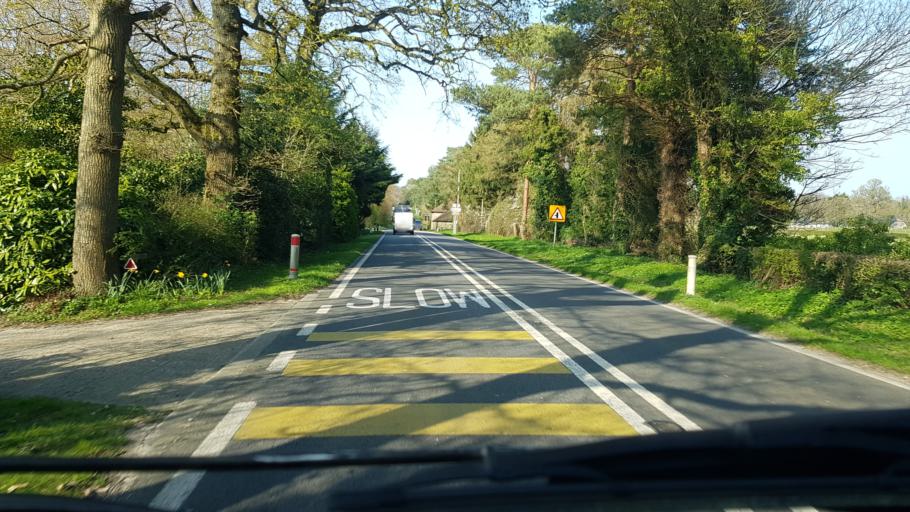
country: GB
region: England
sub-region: West Sussex
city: Petworth
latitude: 50.9560
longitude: -0.6280
